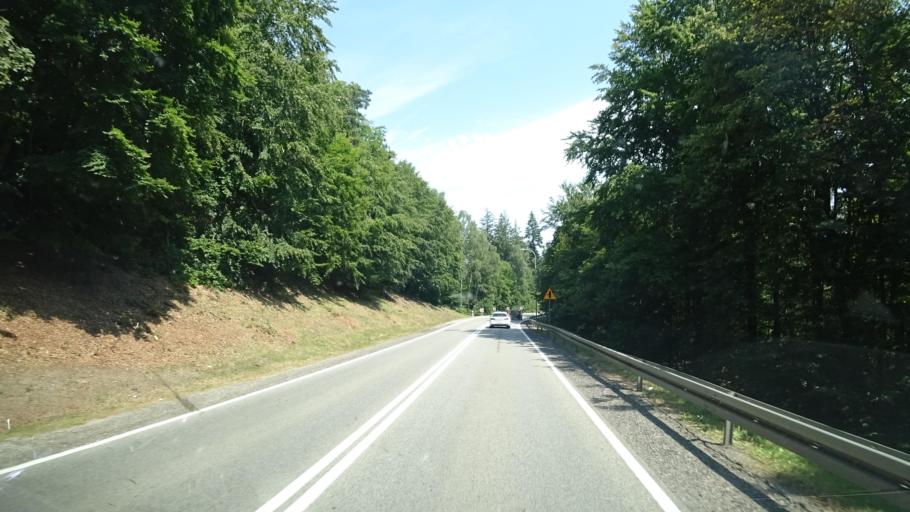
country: PL
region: Pomeranian Voivodeship
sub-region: Powiat koscierski
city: Grabowo Koscierskie
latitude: 54.2196
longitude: 18.1280
